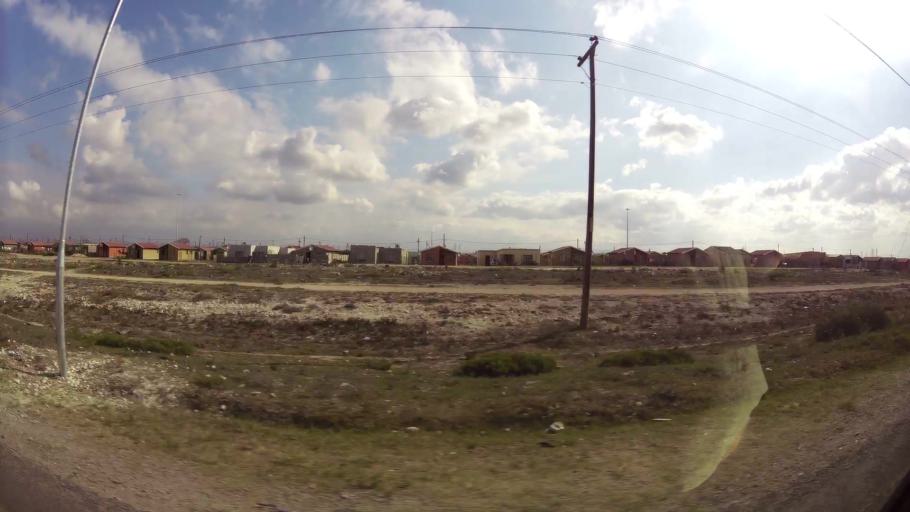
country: ZA
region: Eastern Cape
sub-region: Nelson Mandela Bay Metropolitan Municipality
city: Port Elizabeth
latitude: -33.7719
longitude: 25.5916
